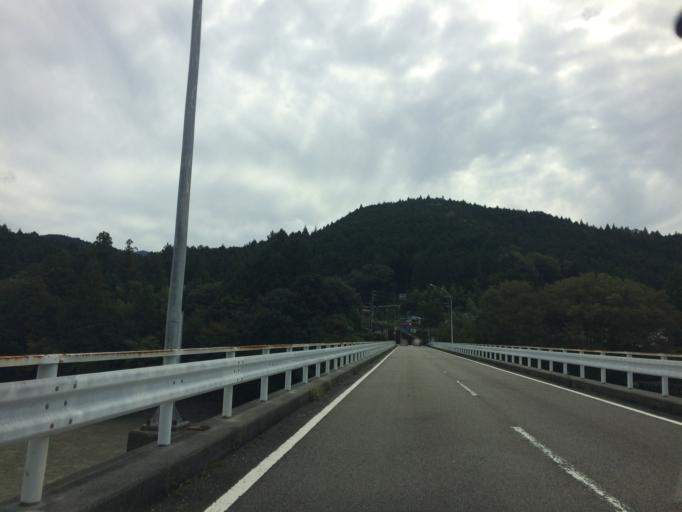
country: JP
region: Shizuoka
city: Fujieda
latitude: 35.1036
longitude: 138.1333
